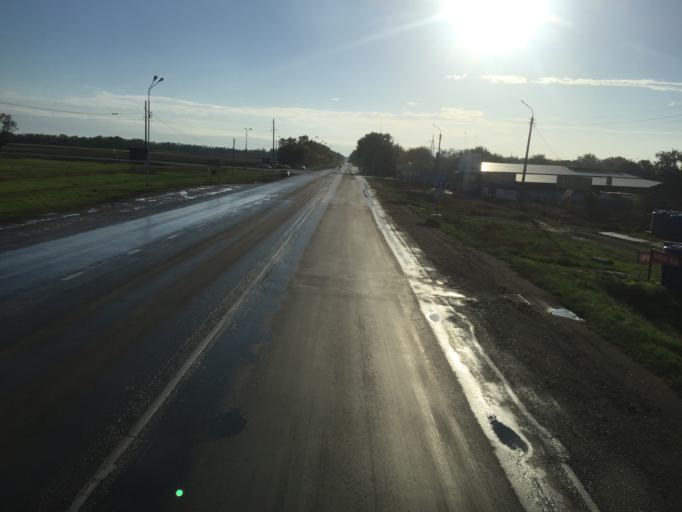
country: RU
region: Rostov
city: Zernograd
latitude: 46.8119
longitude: 40.2969
